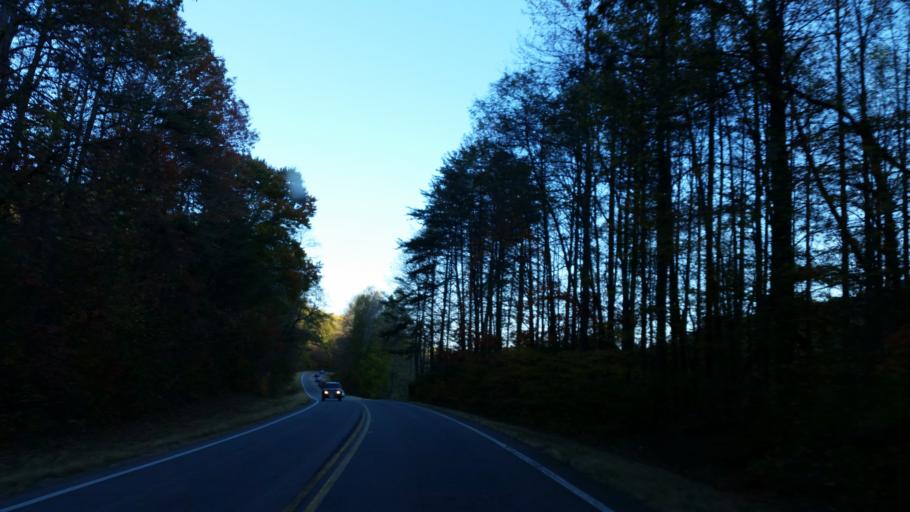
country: US
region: Georgia
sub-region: Pickens County
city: Jasper
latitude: 34.5541
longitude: -84.2929
